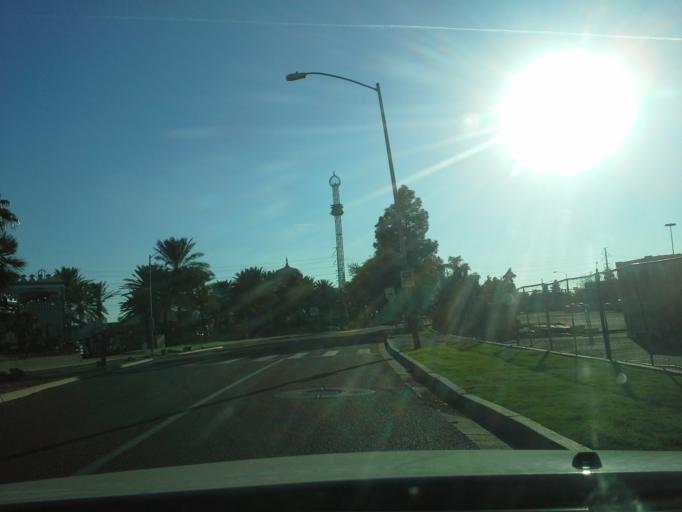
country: US
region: Arizona
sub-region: Maricopa County
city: Glendale
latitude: 33.5730
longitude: -112.1190
